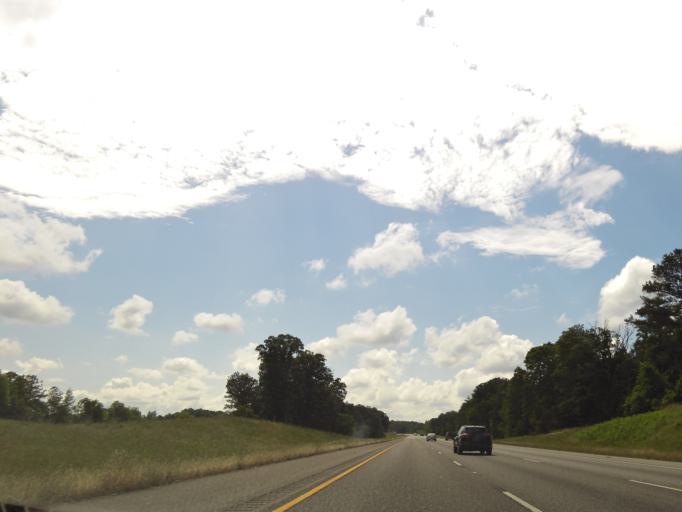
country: US
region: Alabama
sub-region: Calhoun County
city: Bynum
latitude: 33.5815
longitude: -85.9547
